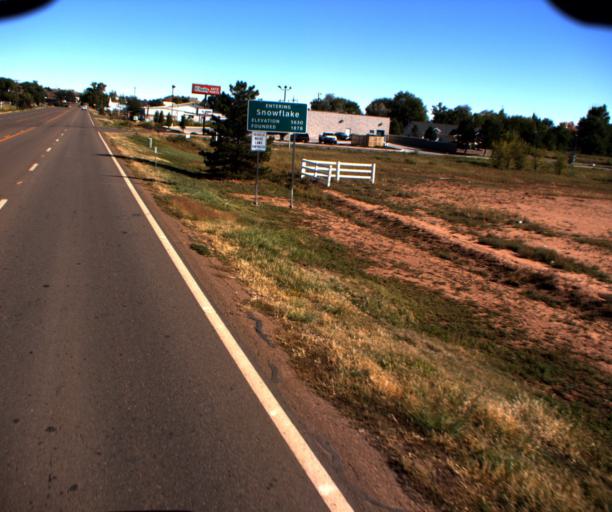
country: US
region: Arizona
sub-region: Navajo County
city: Taylor
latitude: 34.4820
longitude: -110.0838
